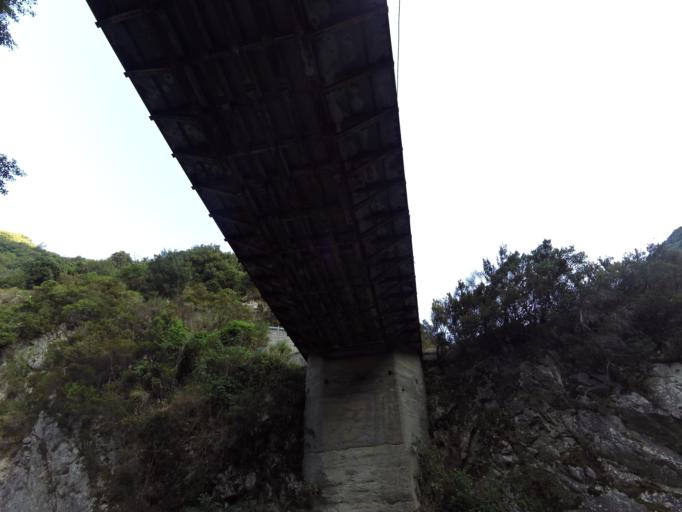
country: IT
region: Calabria
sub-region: Provincia di Vibo-Valentia
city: Nardodipace
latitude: 38.4455
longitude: 16.3420
